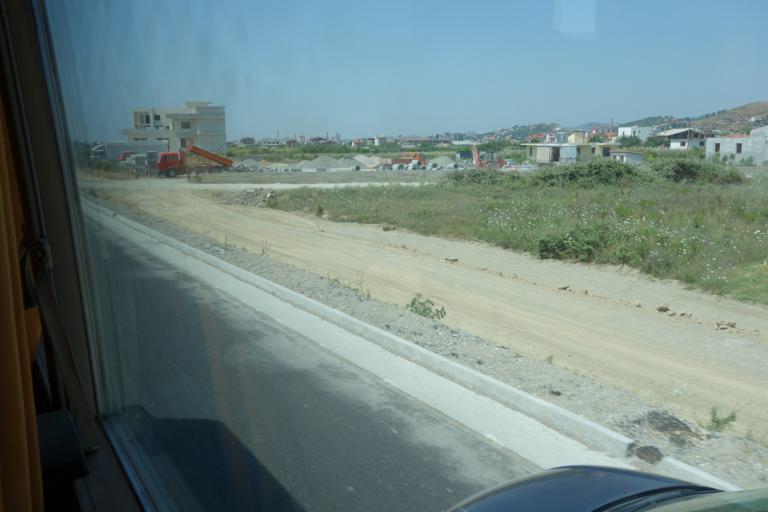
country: AL
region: Tirane
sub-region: Rrethi i Kavajes
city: Kavaje
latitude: 41.1624
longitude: 19.5710
